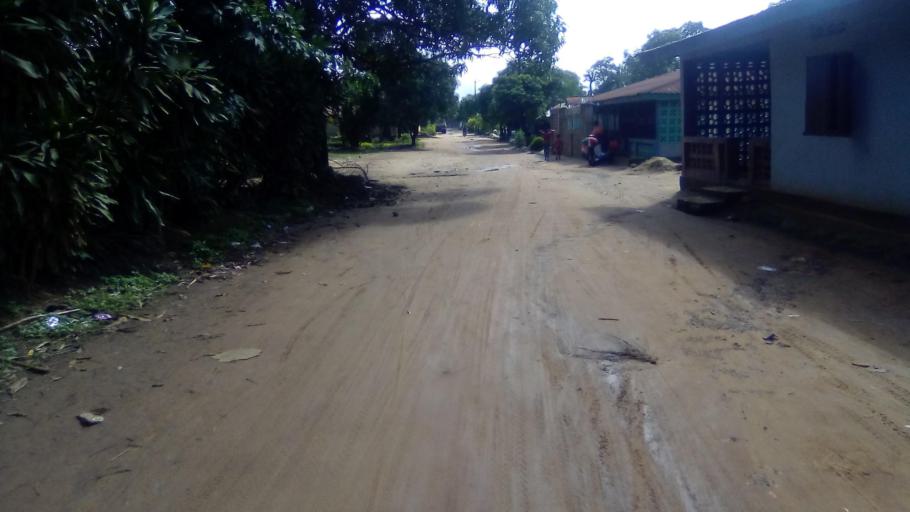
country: SL
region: Southern Province
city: Baoma
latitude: 7.9803
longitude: -11.7265
